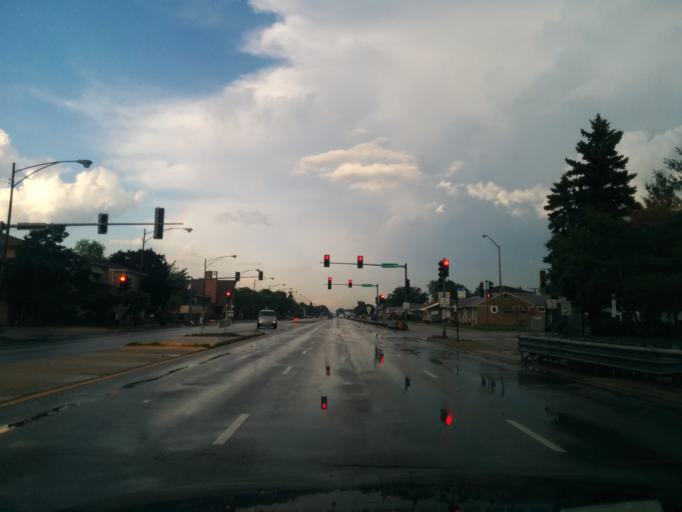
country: US
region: Illinois
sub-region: Cook County
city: Hometown
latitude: 41.7346
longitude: -87.7324
